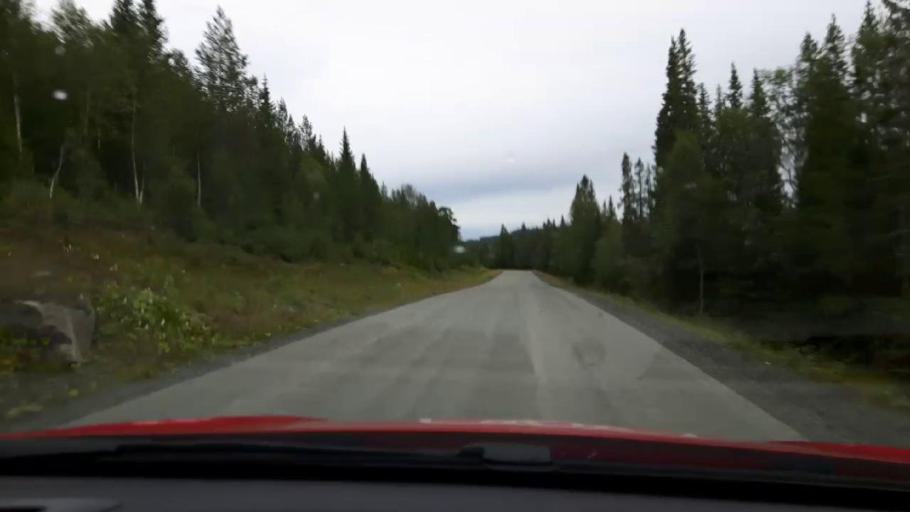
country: SE
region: Jaemtland
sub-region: Are Kommun
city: Are
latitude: 63.4351
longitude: 13.2687
